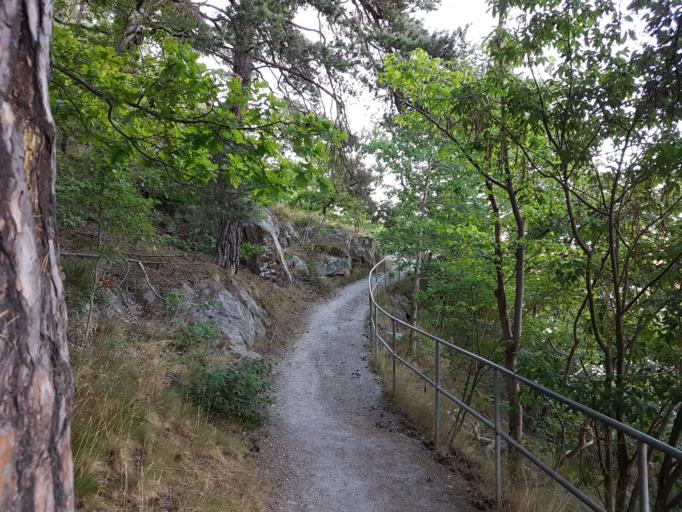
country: SE
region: Stockholm
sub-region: Sundbybergs Kommun
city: Sundbyberg
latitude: 59.3253
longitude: 17.9838
